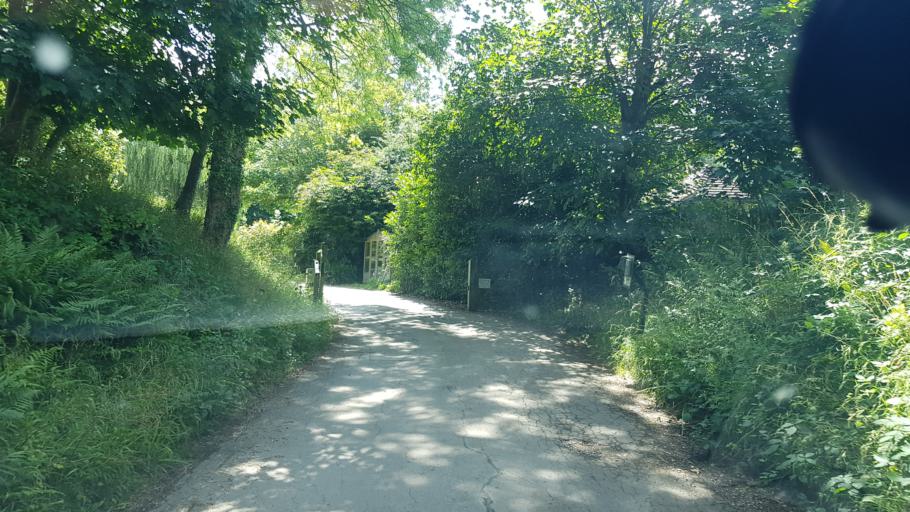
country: GB
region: England
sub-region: Kent
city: Edenbridge
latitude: 51.1872
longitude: 0.1410
